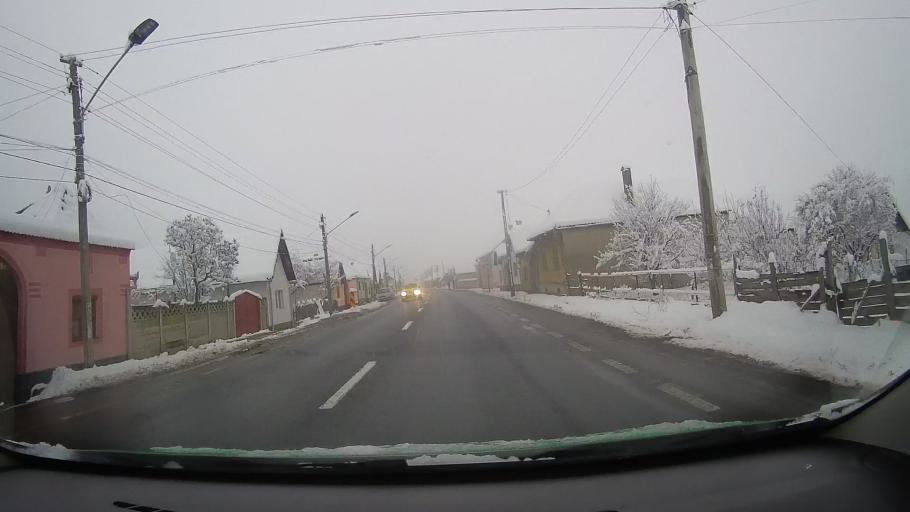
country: RO
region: Sibiu
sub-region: Comuna Orlat
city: Orlat
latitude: 45.7845
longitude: 23.9373
